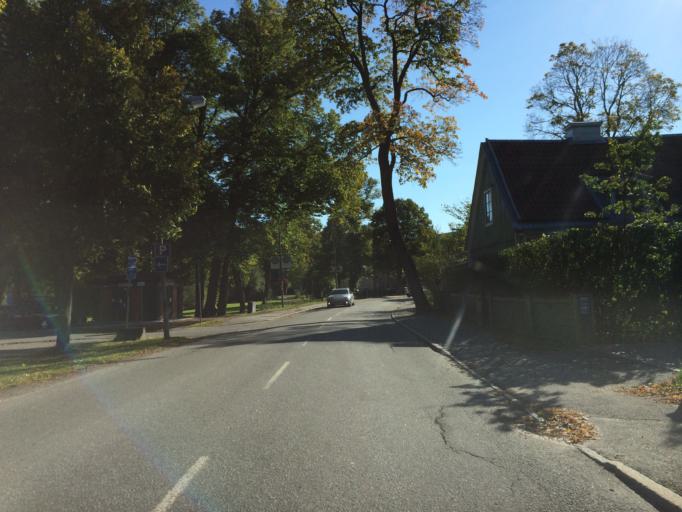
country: SE
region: Stockholm
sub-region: Lidingo
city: Lidingoe
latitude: 59.3312
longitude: 18.1318
